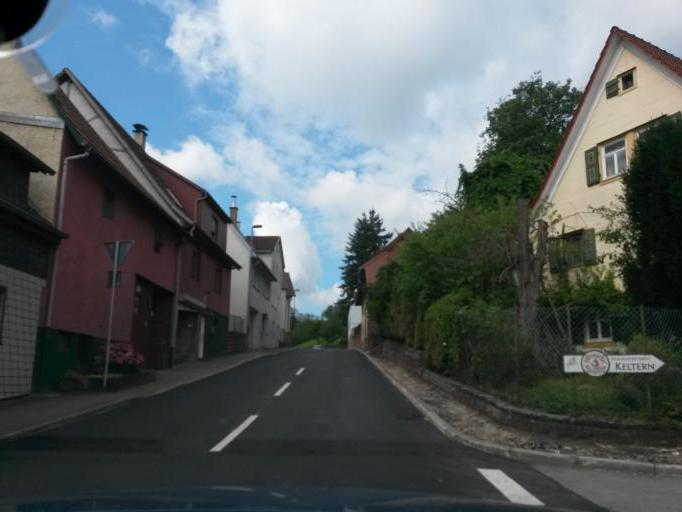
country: DE
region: Baden-Wuerttemberg
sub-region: Karlsruhe Region
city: Neuenburg
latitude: 48.8891
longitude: 8.5450
